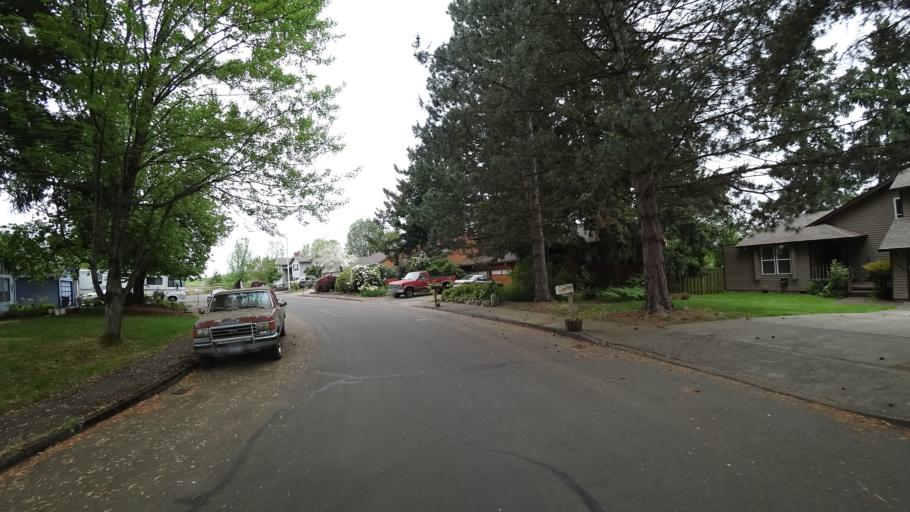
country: US
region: Oregon
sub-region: Washington County
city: Hillsboro
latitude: 45.4985
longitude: -122.9707
